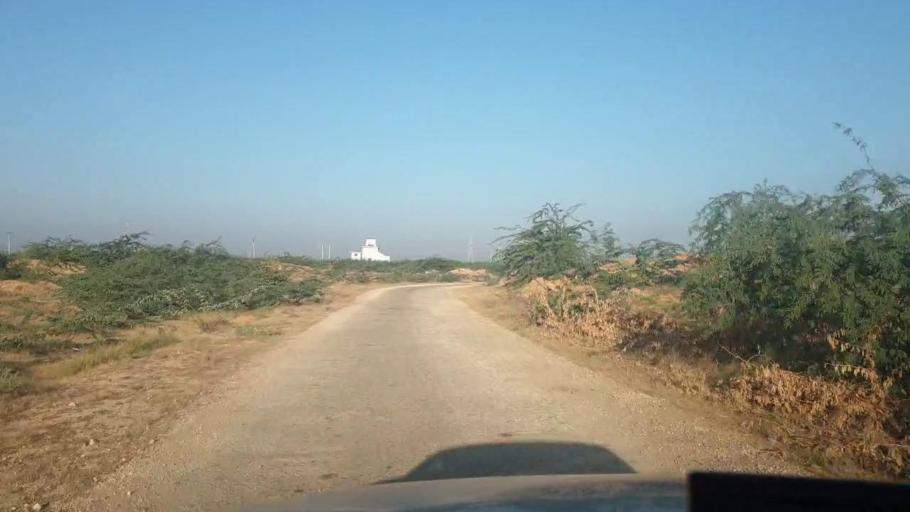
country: PK
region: Sindh
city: Thatta
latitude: 24.6982
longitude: 67.8579
